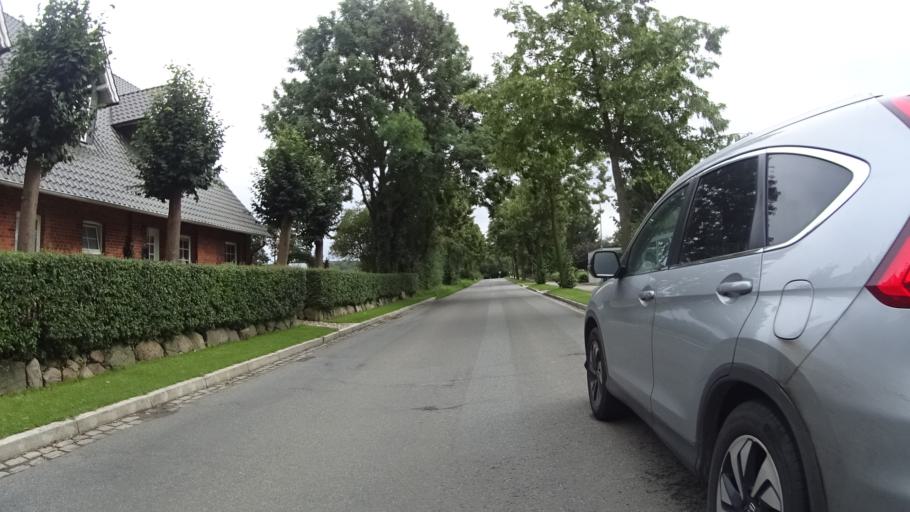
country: DE
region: Schleswig-Holstein
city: Duvensee
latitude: 53.6920
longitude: 10.5689
